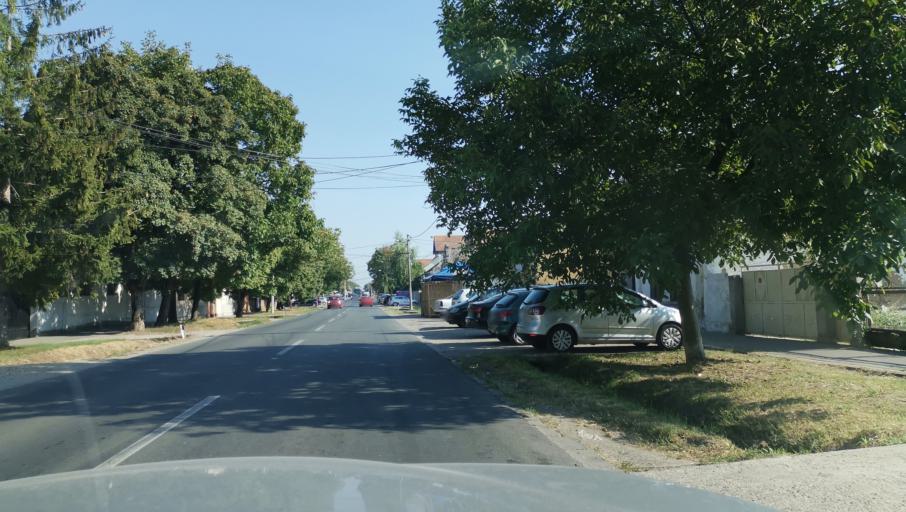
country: RS
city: Dobanovci
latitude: 44.8296
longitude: 20.2213
